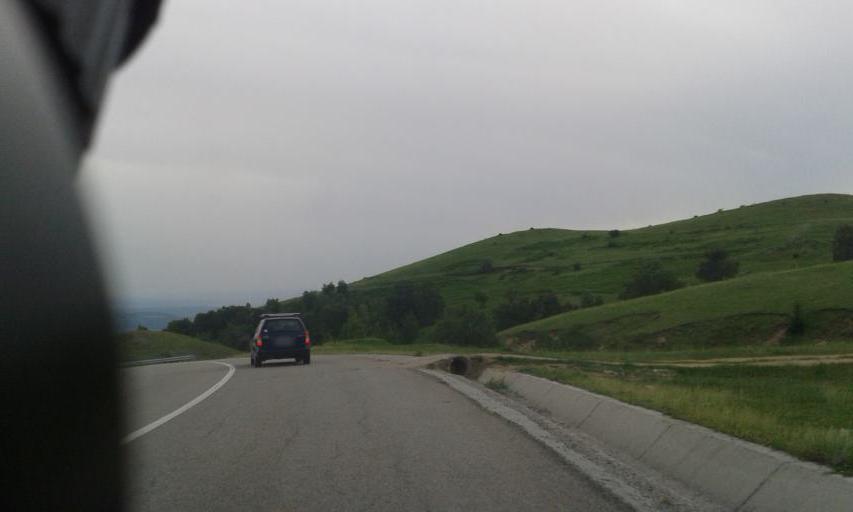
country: RO
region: Gorj
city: Novaci-Straini
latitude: 45.2178
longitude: 23.6987
